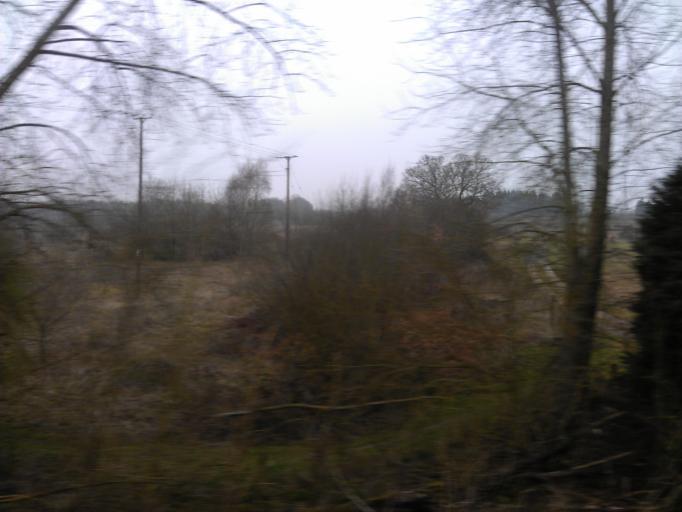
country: GB
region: England
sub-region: Essex
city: Alresford
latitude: 51.8544
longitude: 0.9893
